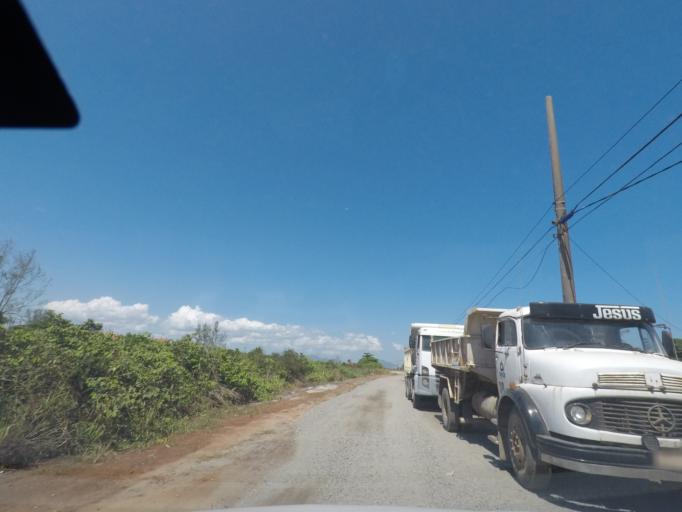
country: BR
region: Rio de Janeiro
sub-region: Marica
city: Marica
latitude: -22.9701
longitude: -42.9072
